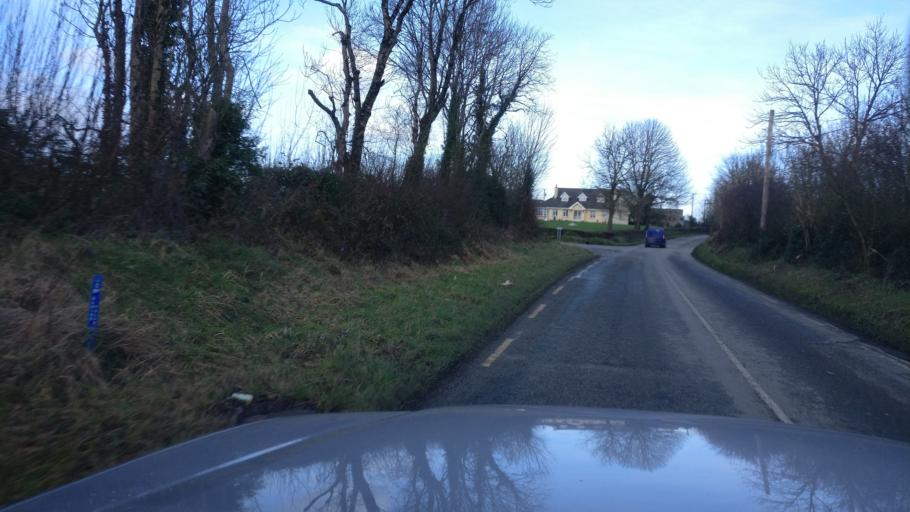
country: IE
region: Leinster
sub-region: Kilkenny
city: Castlecomer
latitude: 52.8363
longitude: -7.1932
